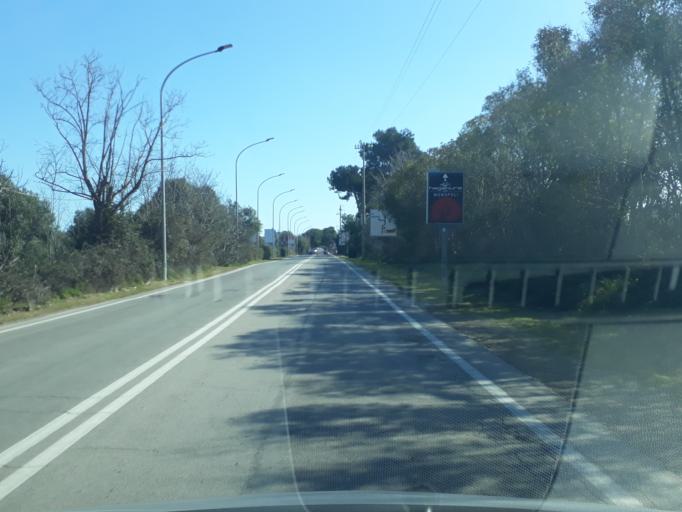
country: IT
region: Apulia
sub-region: Provincia di Bari
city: Monopoli
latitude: 40.9637
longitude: 17.2777
